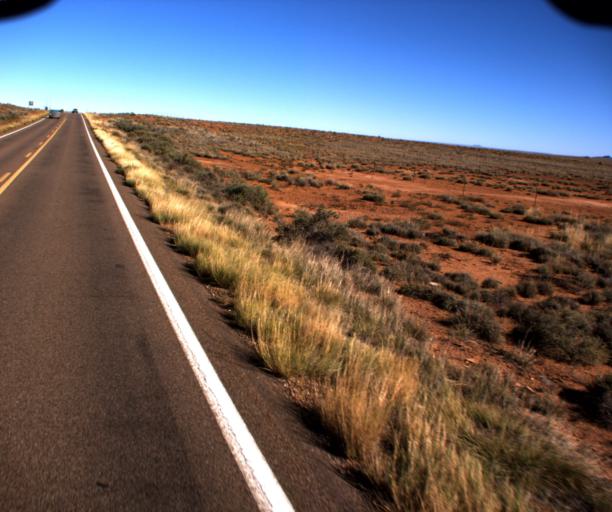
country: US
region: Arizona
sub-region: Navajo County
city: Holbrook
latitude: 34.7157
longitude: -110.1127
